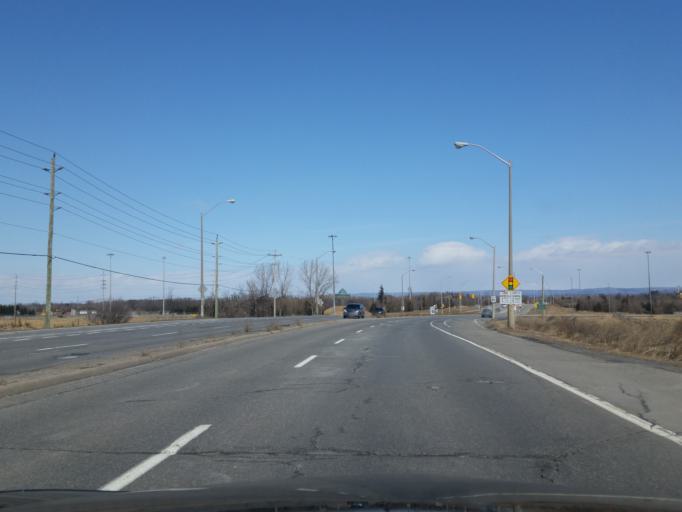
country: CA
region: Ontario
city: Bells Corners
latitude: 45.3342
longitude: -75.8401
